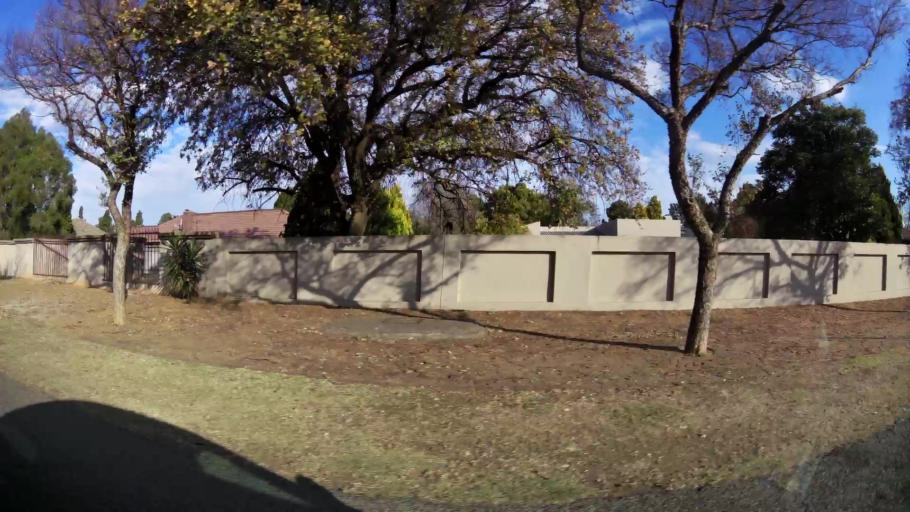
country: ZA
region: Orange Free State
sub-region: Lejweleputswa District Municipality
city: Welkom
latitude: -27.9867
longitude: 26.7231
